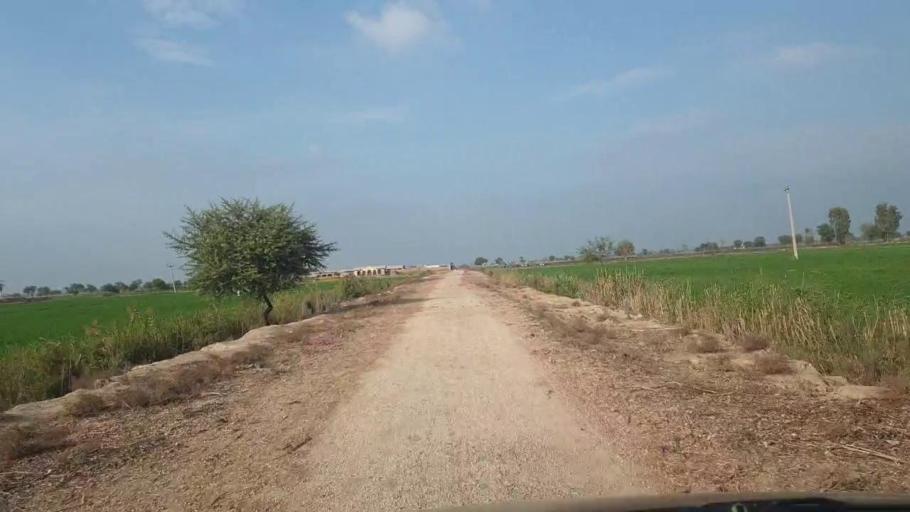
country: PK
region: Sindh
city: Shahdadpur
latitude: 25.8965
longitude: 68.6707
